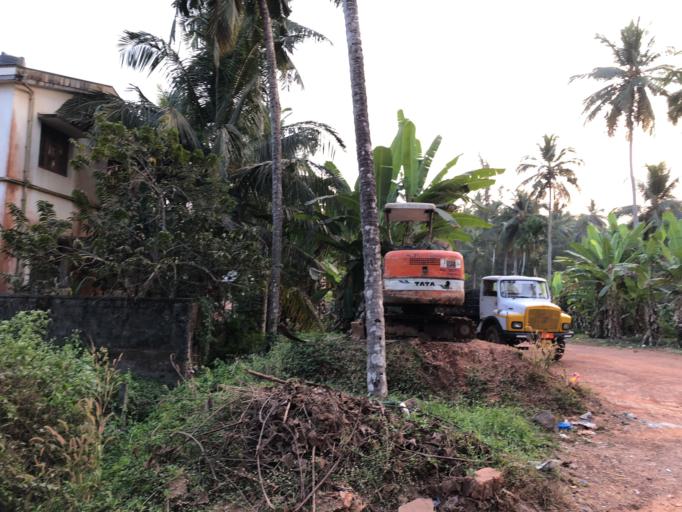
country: IN
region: Karnataka
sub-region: Dakshina Kannada
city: Mangalore
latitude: 12.8886
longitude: 74.8678
